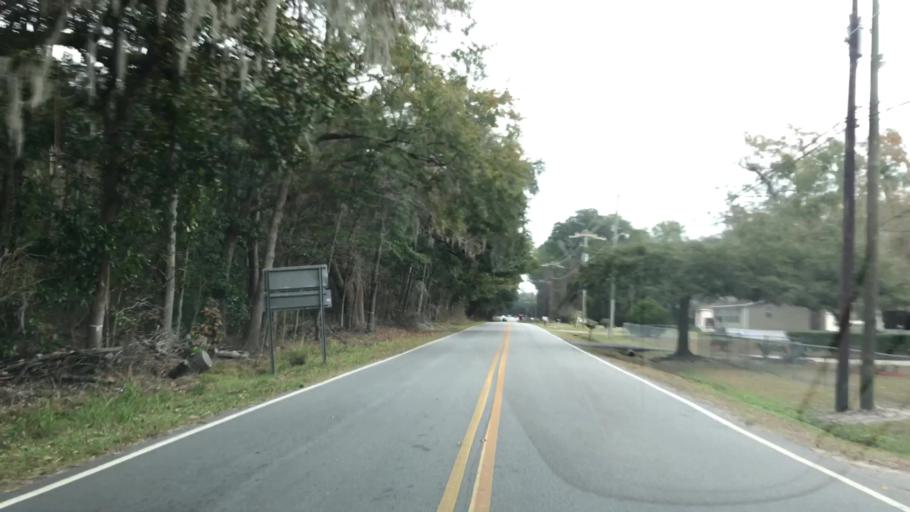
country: US
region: South Carolina
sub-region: Beaufort County
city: Burton
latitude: 32.4189
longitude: -80.7376
